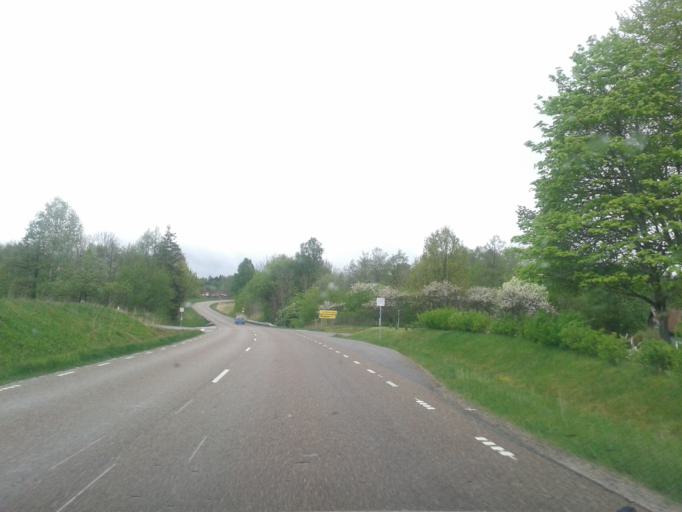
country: SE
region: Vaestra Goetaland
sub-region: Lilla Edets Kommun
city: Lodose
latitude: 58.0629
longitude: 12.1337
